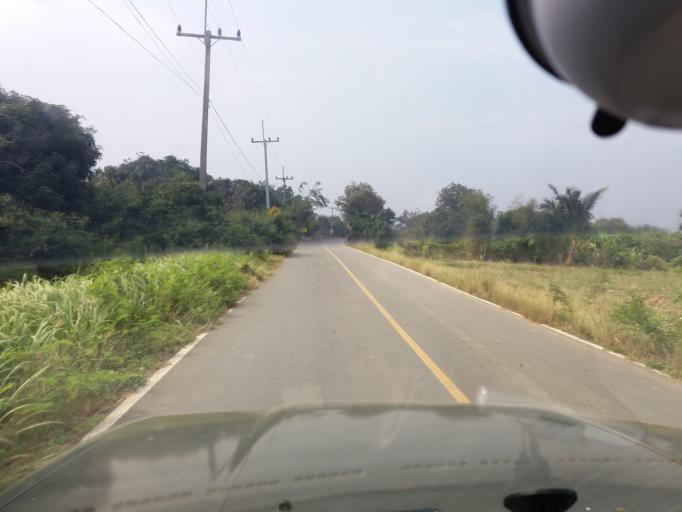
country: TH
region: Suphan Buri
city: Doem Bang Nang Buat
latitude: 14.8933
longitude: 100.1815
